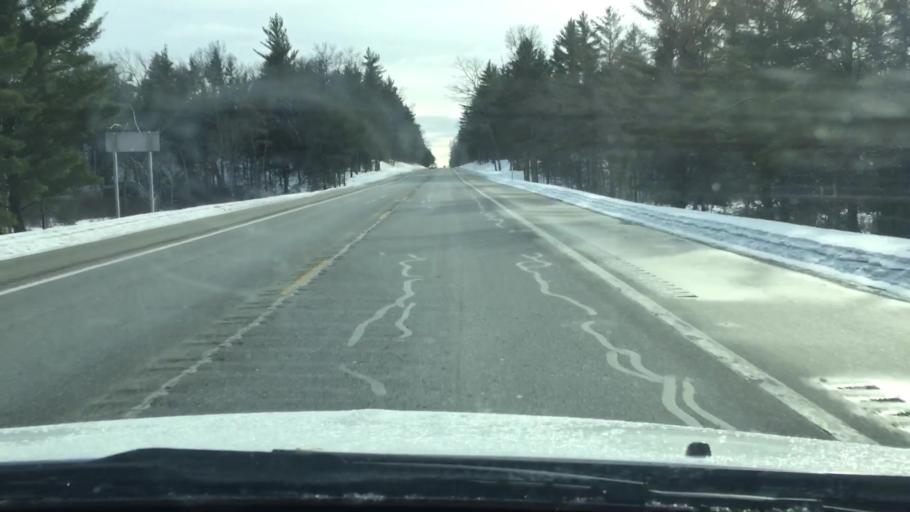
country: US
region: Michigan
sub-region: Wexford County
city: Manton
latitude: 44.5629
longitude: -85.3670
